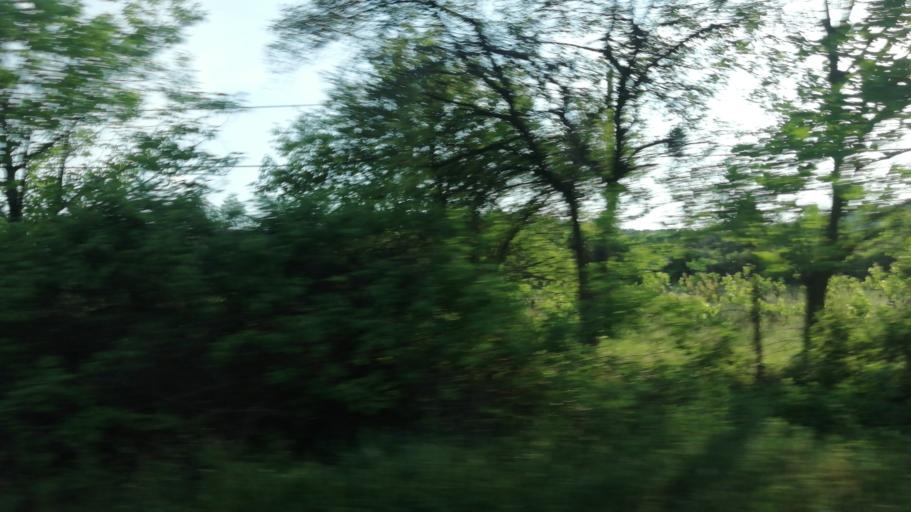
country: TR
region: Karabuk
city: Karabuk
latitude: 41.1395
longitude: 32.6310
